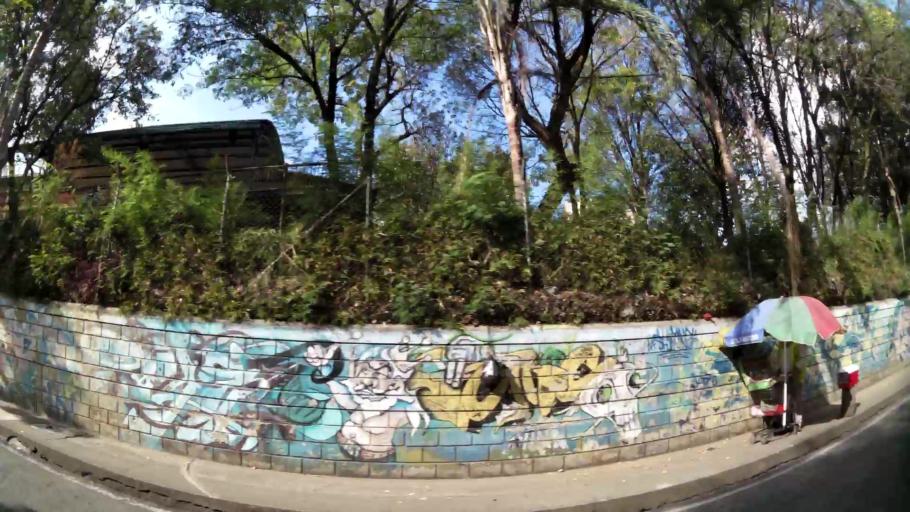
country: CO
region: Antioquia
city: Medellin
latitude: 6.2823
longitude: -75.5725
